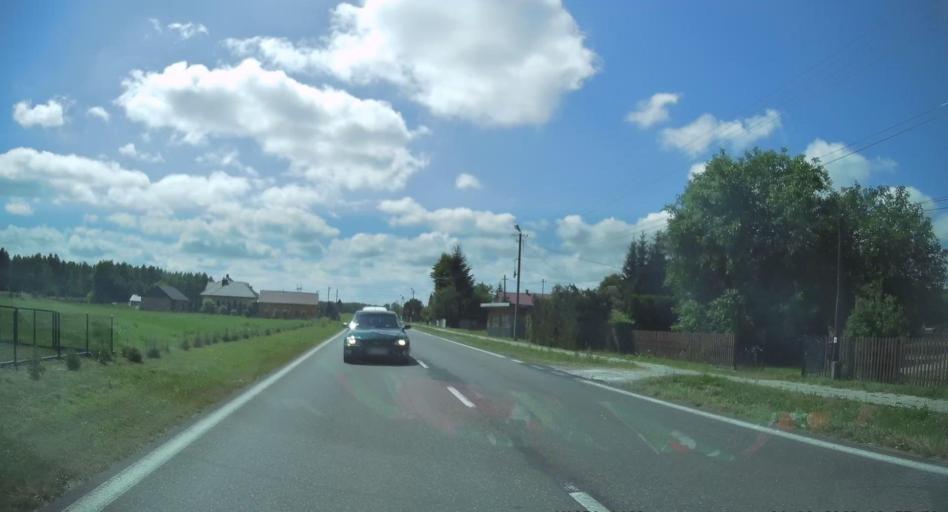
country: PL
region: Subcarpathian Voivodeship
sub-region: Powiat mielecki
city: Padew Narodowa
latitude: 50.4160
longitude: 21.4798
